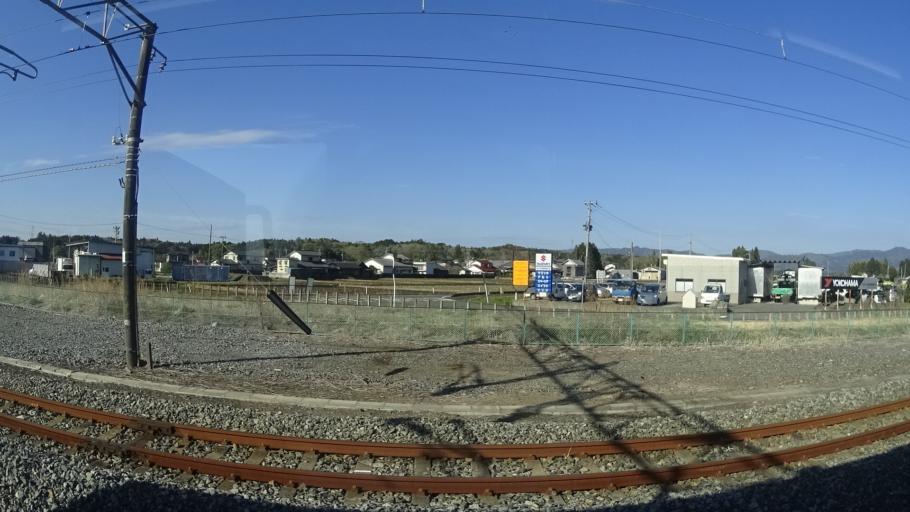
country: JP
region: Fukushima
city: Namie
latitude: 37.6056
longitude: 140.9908
